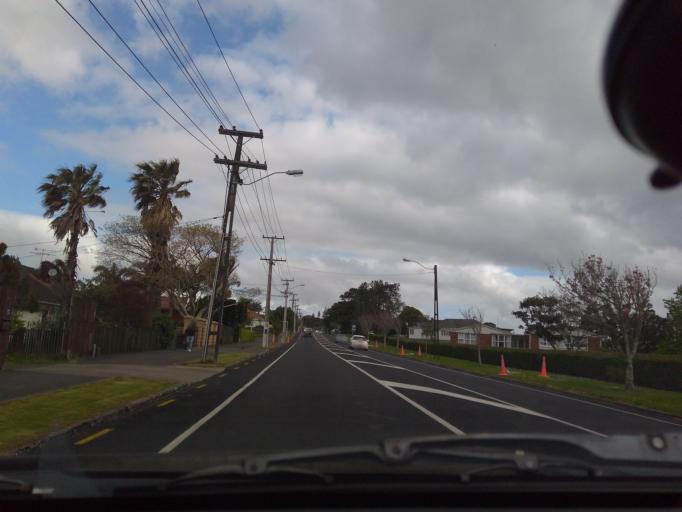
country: NZ
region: Auckland
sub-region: Auckland
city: Rosebank
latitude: -36.8753
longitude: 174.7103
